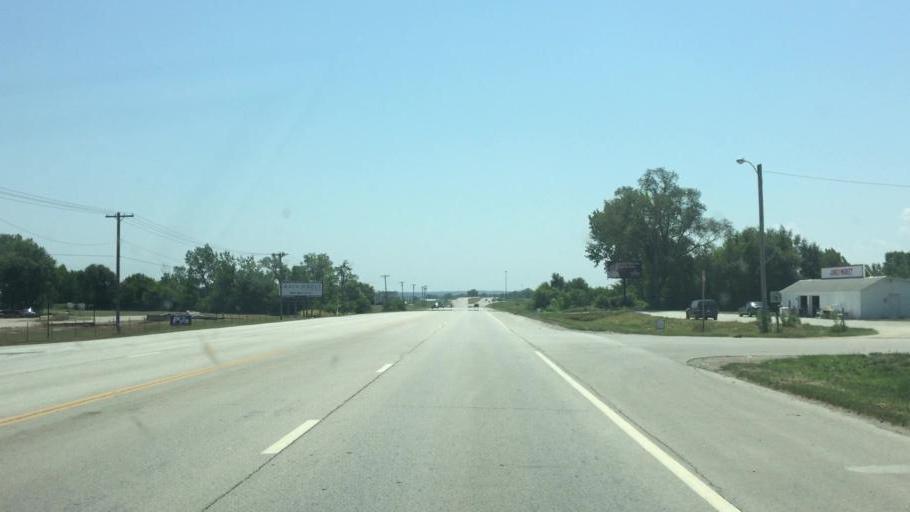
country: US
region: Kansas
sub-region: Doniphan County
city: Wathena
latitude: 39.7543
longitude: -94.9362
